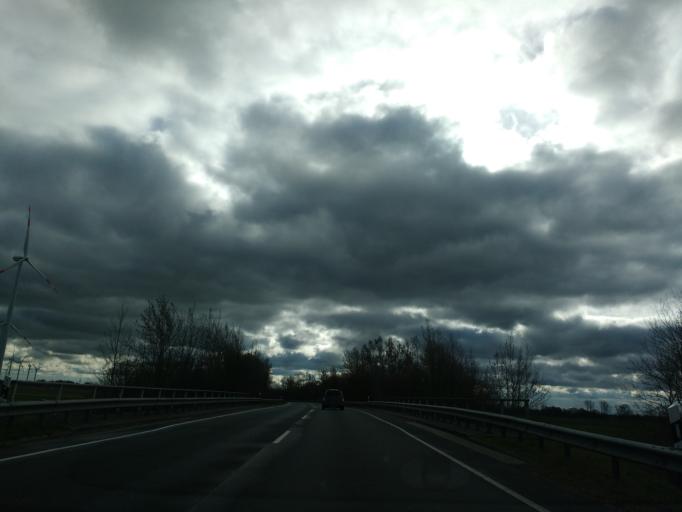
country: DE
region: Lower Saxony
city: Cuxhaven
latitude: 53.8251
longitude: 8.6826
